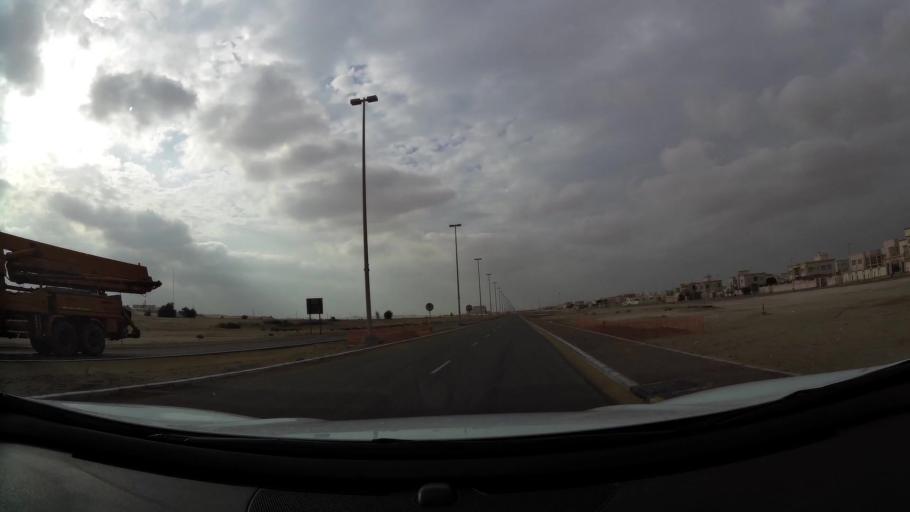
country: AE
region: Abu Dhabi
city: Abu Dhabi
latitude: 24.3356
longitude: 54.6244
